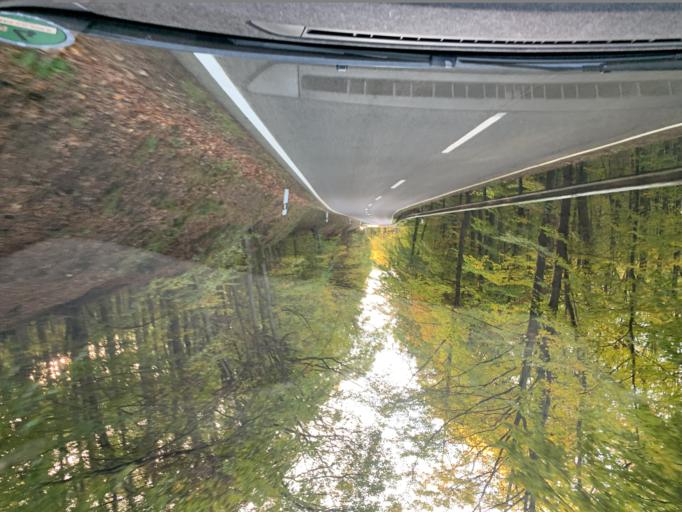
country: DE
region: North Rhine-Westphalia
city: Heimbach
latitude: 50.6248
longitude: 6.4812
